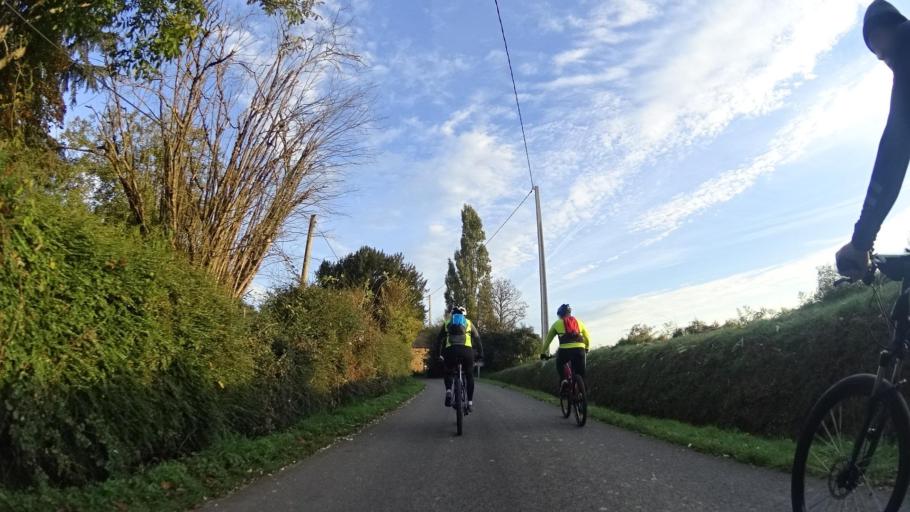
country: FR
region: Brittany
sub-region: Departement des Cotes-d'Armor
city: Evran
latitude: 48.3491
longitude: -1.9405
